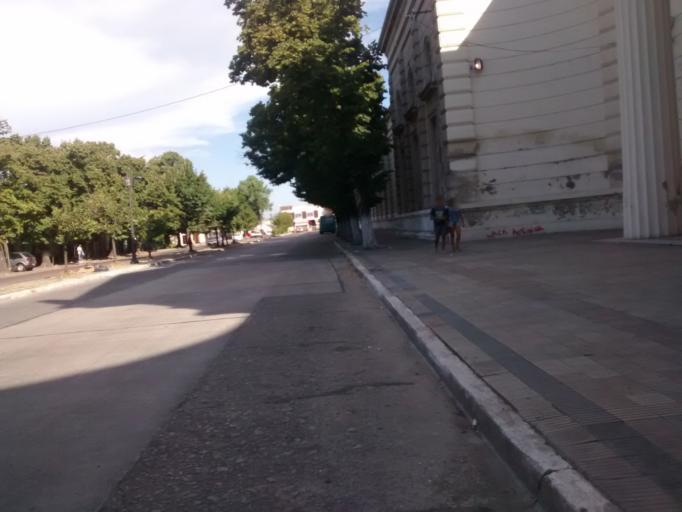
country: AR
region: Buenos Aires
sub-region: Partido de La Plata
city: La Plata
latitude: -34.9553
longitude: -57.9503
